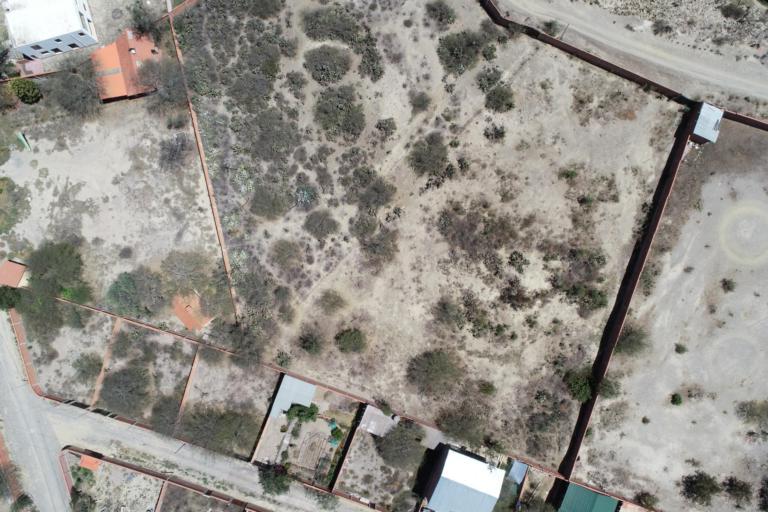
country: BO
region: La Paz
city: La Paz
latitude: -16.6484
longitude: -68.0441
